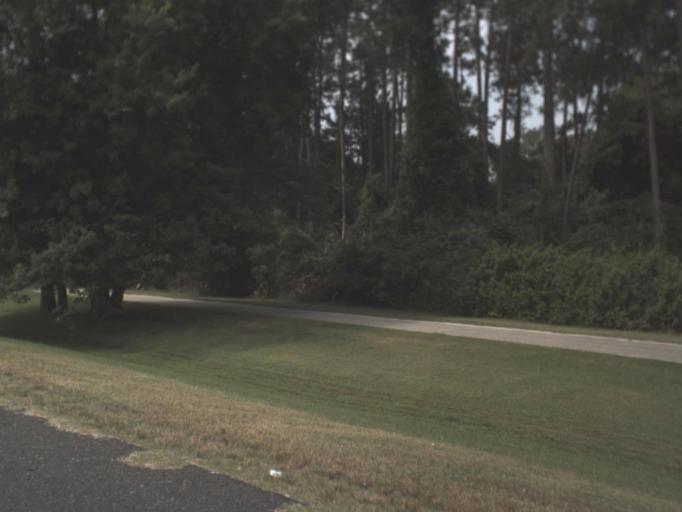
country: US
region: Florida
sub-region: Clay County
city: Orange Park
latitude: 30.1201
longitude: -81.7048
